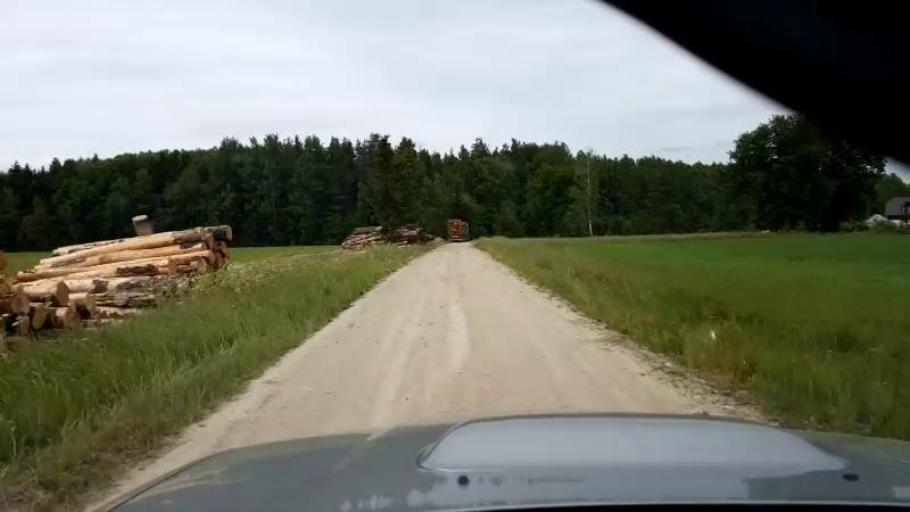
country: EE
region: Paernumaa
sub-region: Sindi linn
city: Sindi
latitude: 58.5183
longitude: 24.6176
